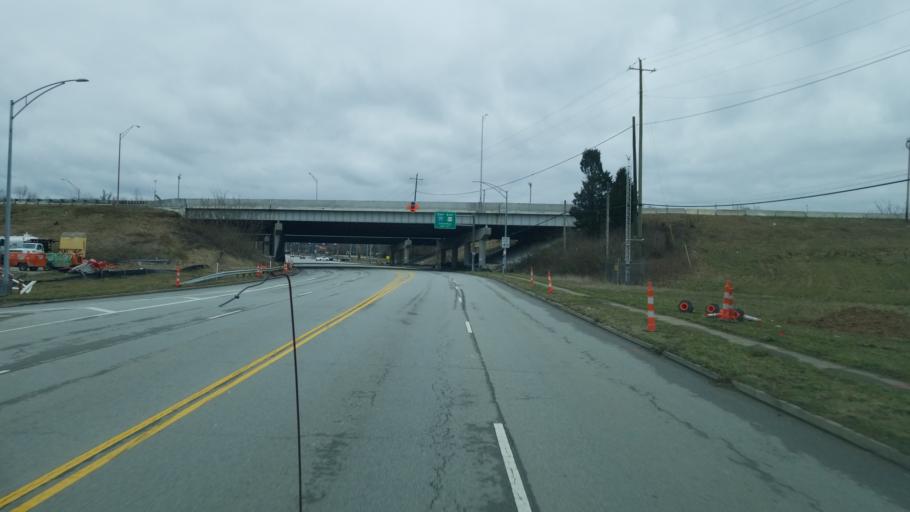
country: US
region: Kentucky
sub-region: Campbell County
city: Fort Thomas
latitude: 39.0618
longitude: -84.4222
